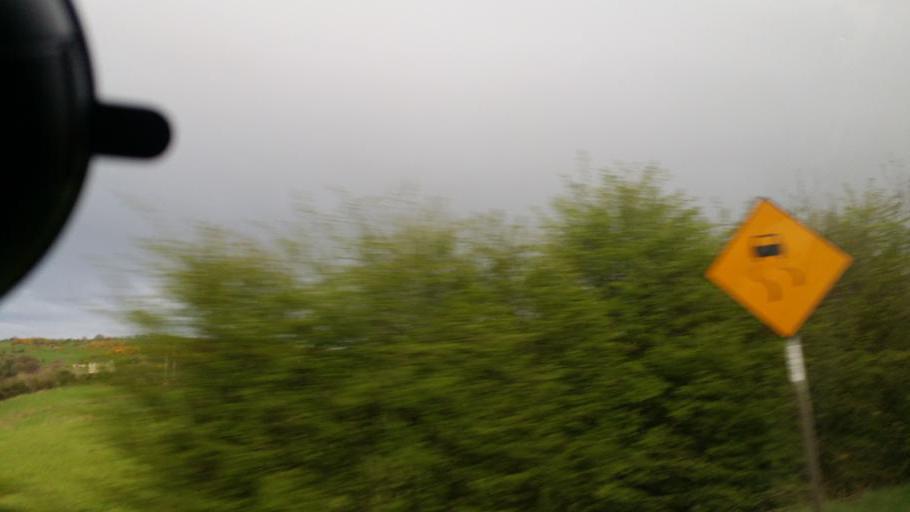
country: IE
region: Ulster
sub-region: An Cabhan
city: Virginia
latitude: 53.8526
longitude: -7.1024
